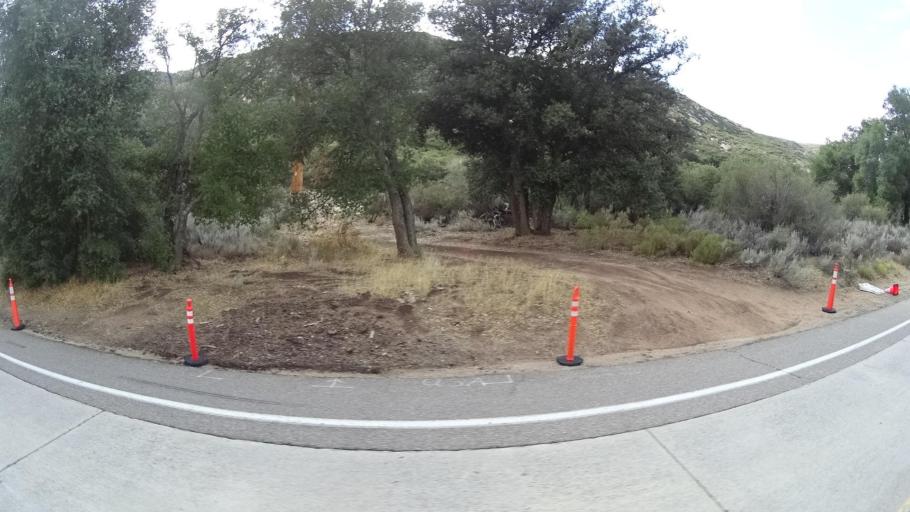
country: US
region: California
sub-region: San Diego County
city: Pine Valley
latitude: 32.7986
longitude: -116.4990
